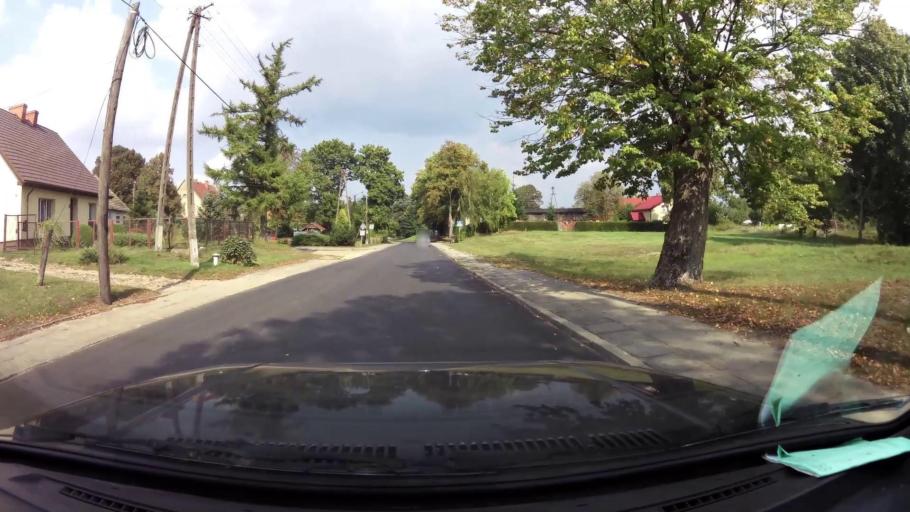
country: PL
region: Pomeranian Voivodeship
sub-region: Powiat slupski
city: Kepice
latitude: 54.1655
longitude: 16.8205
